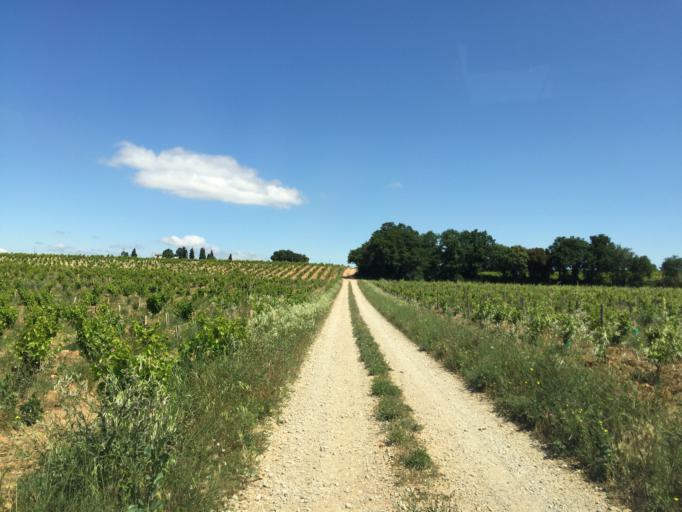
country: FR
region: Provence-Alpes-Cote d'Azur
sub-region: Departement du Vaucluse
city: Bedarrides
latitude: 44.0454
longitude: 4.8730
